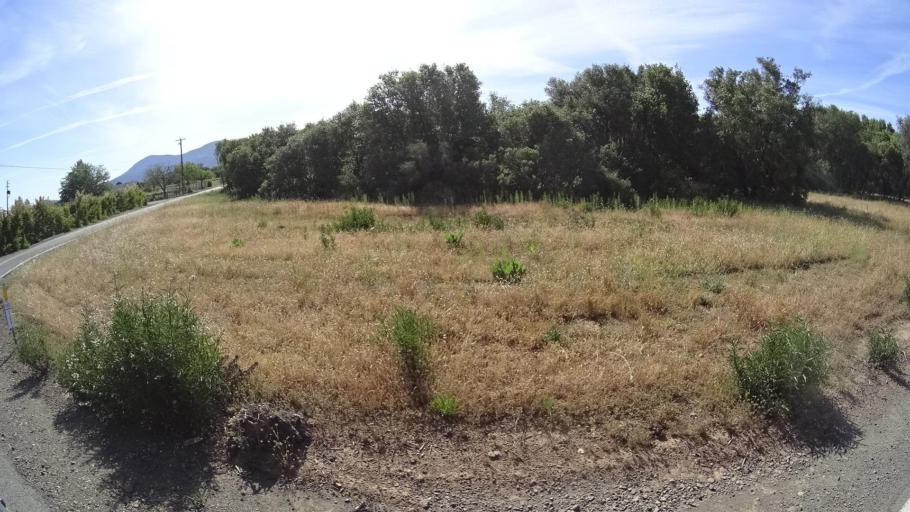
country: US
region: California
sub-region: Lake County
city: Kelseyville
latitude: 38.9643
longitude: -122.8809
